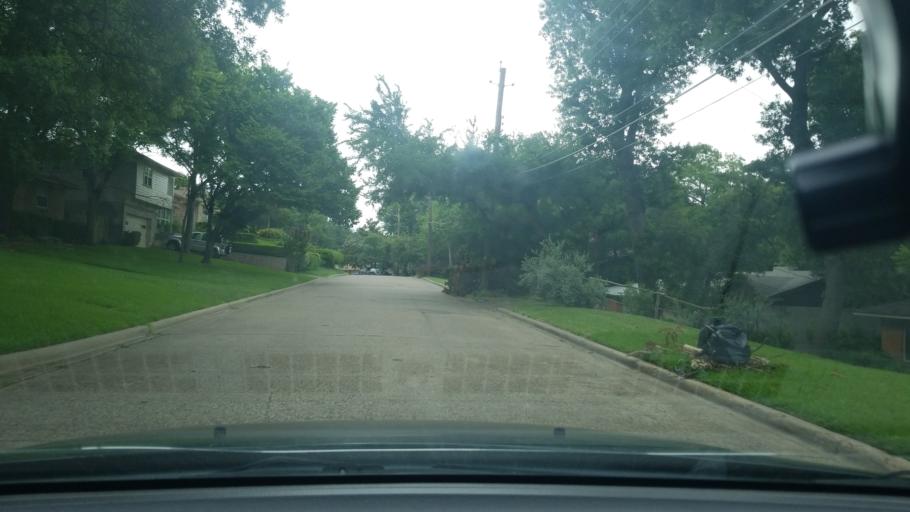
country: US
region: Texas
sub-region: Dallas County
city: Balch Springs
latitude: 32.7652
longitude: -96.6930
